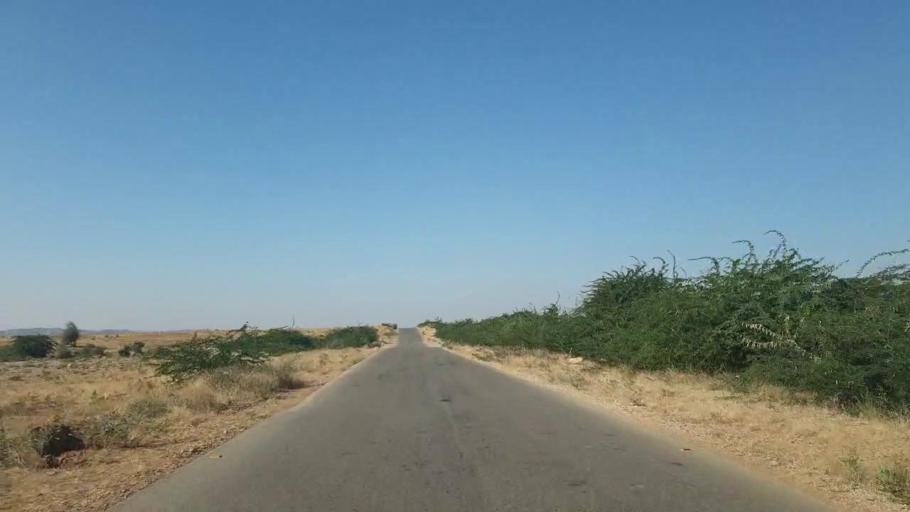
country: PK
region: Sindh
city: Malir Cantonment
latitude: 25.2640
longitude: 67.5974
